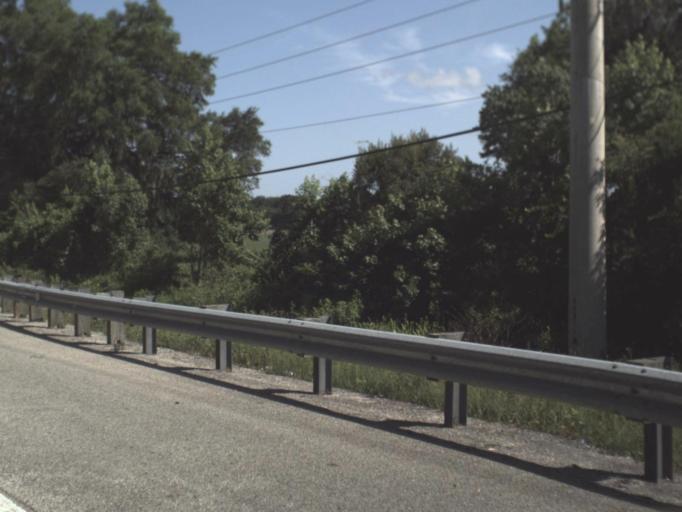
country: US
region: Florida
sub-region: Saint Johns County
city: Saint Augustine
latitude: 29.9535
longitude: -81.4567
